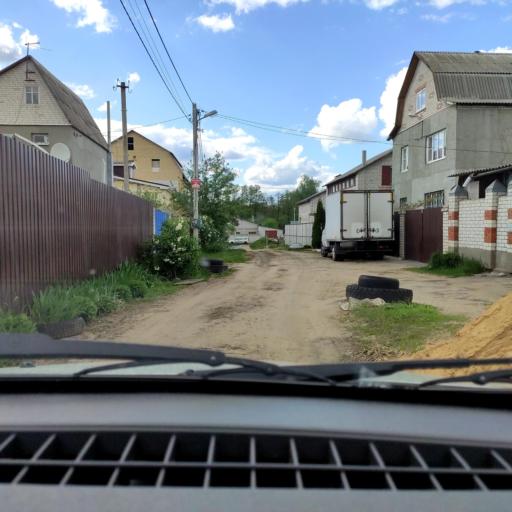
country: RU
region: Voronezj
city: Pridonskoy
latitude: 51.6168
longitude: 39.0571
